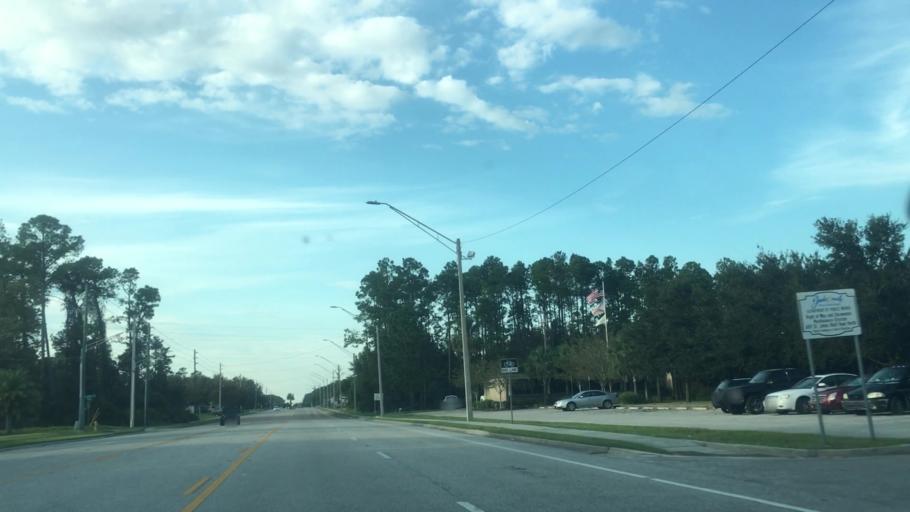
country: US
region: Florida
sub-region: Duval County
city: Atlantic Beach
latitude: 30.3318
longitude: -81.5232
